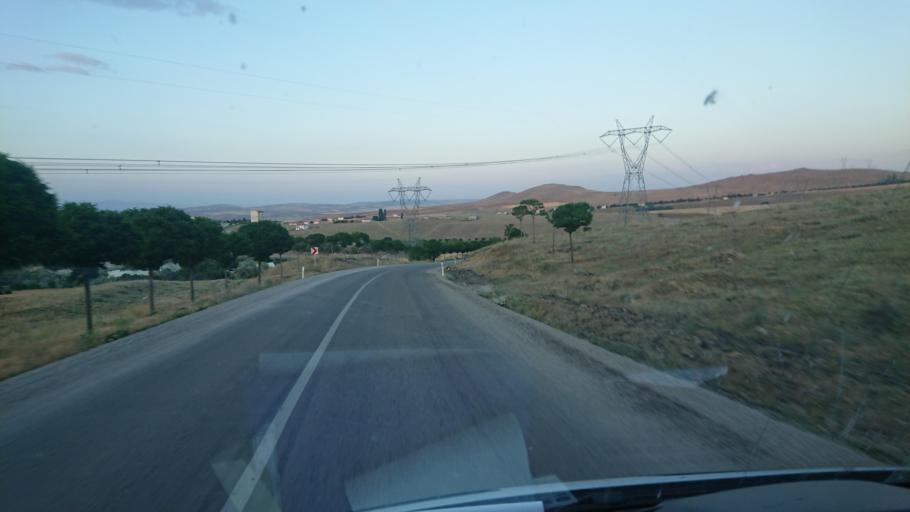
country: TR
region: Aksaray
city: Sariyahsi
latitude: 38.9706
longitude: 33.8224
